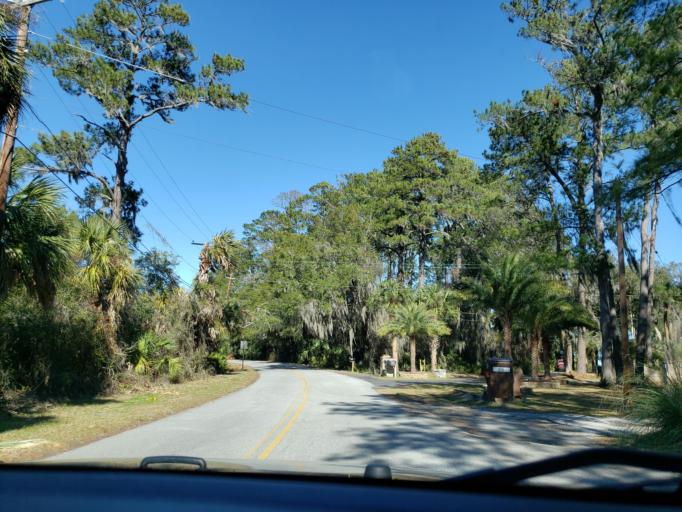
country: US
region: Georgia
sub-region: Chatham County
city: Whitemarsh Island
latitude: 32.0507
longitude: -81.0082
